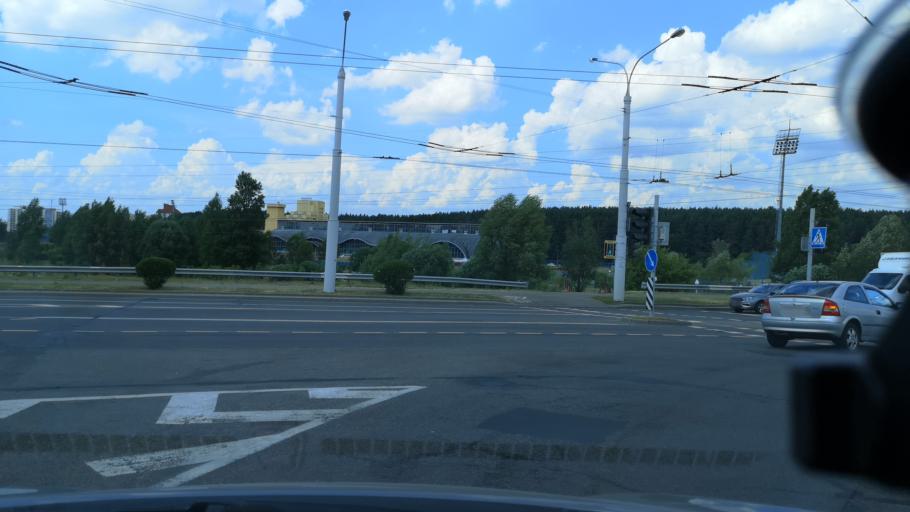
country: BY
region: Minsk
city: Borovlyany
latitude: 53.9421
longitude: 27.6521
